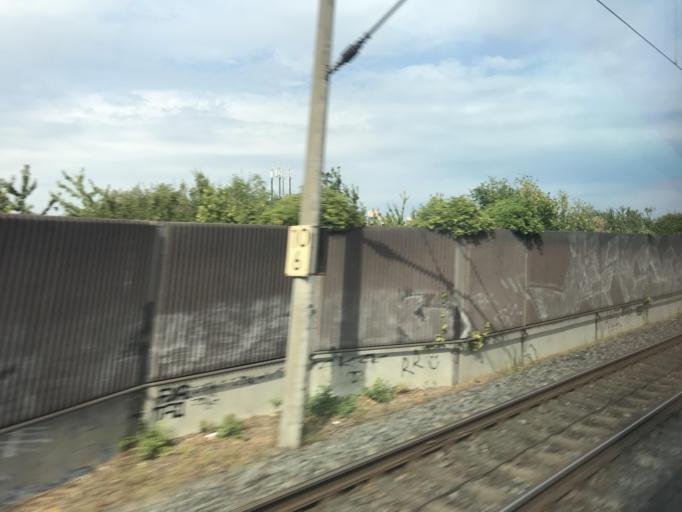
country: DE
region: North Rhine-Westphalia
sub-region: Regierungsbezirk Koln
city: Frechen
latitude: 50.9416
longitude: 6.8208
